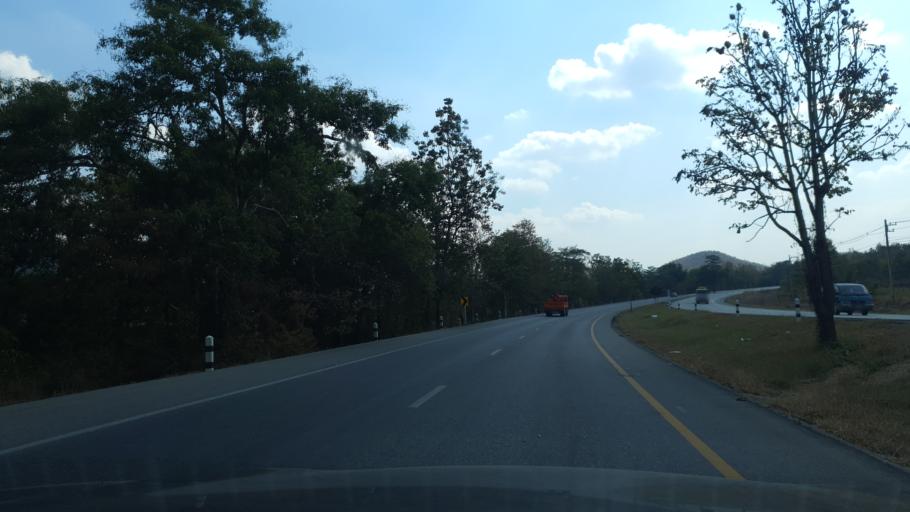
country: TH
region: Lampang
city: Mae Phrik
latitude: 17.3363
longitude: 99.1532
